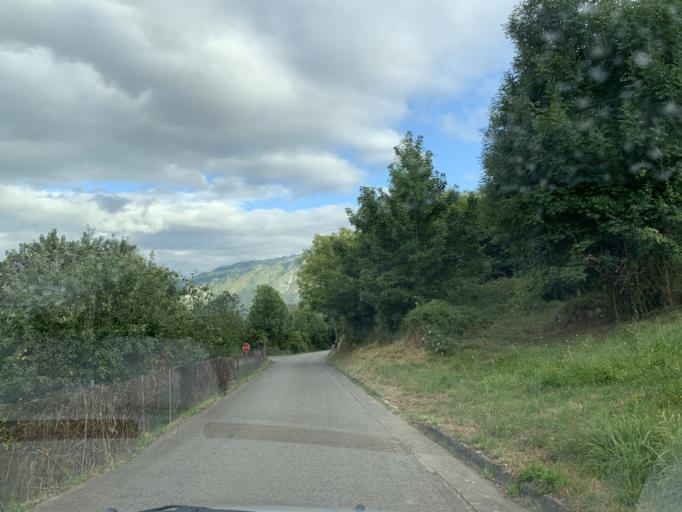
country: ES
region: Asturias
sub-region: Province of Asturias
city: Carrena
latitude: 43.3231
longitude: -4.8626
